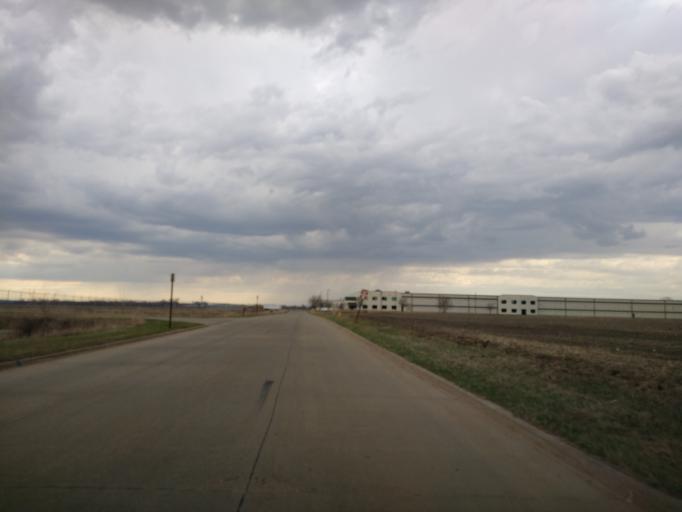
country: US
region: Iowa
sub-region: Woodbury County
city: Sergeant Bluff
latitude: 42.4148
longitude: -96.3729
